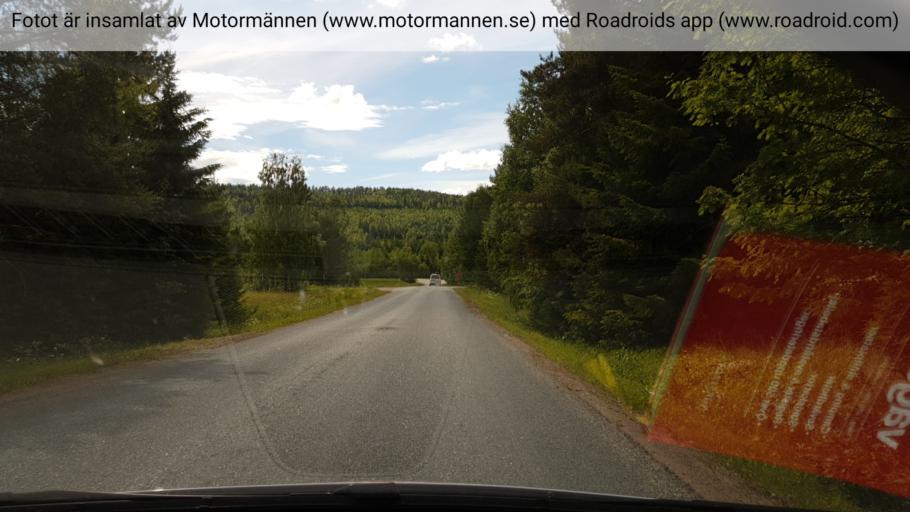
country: SE
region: Vaesternorrland
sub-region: Solleftea Kommun
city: Solleftea
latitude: 63.3132
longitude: 17.2047
